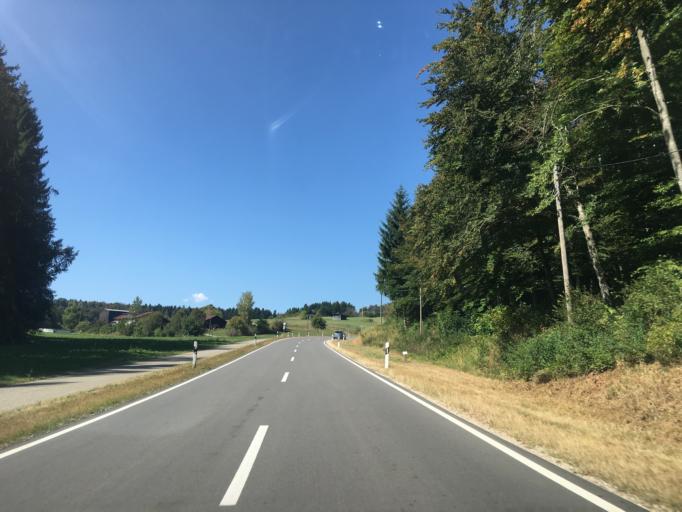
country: DE
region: Baden-Wuerttemberg
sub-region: Tuebingen Region
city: Munsingen
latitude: 48.3835
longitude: 9.4865
